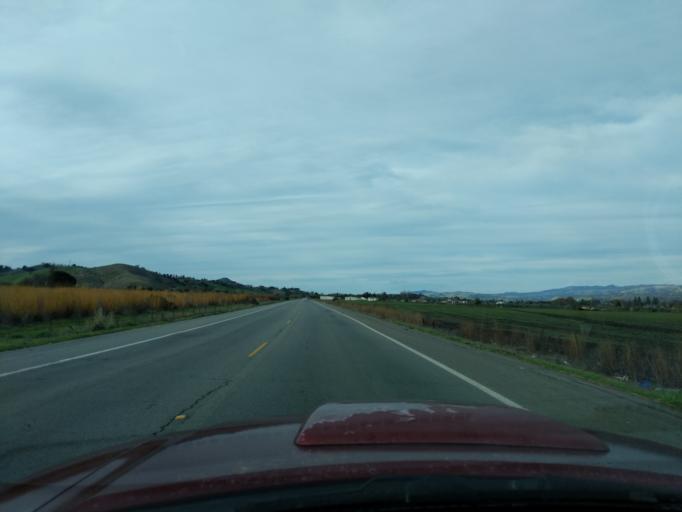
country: US
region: California
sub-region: Santa Clara County
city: San Martin
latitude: 37.0599
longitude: -121.6089
